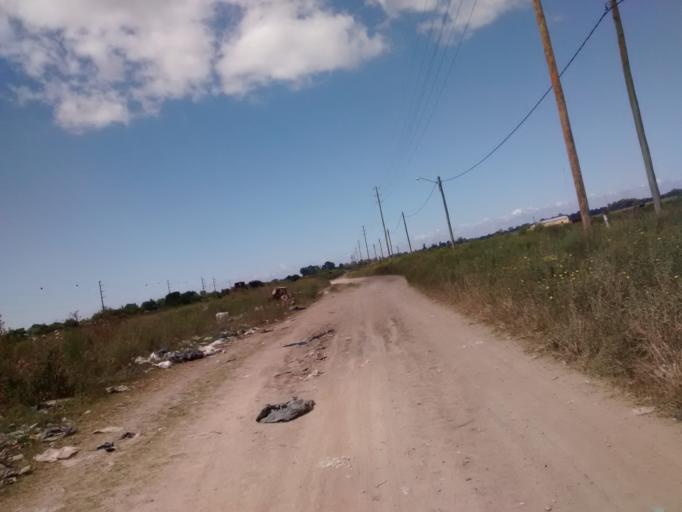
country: AR
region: Buenos Aires
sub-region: Partido de La Plata
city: La Plata
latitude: -34.9693
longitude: -57.9373
